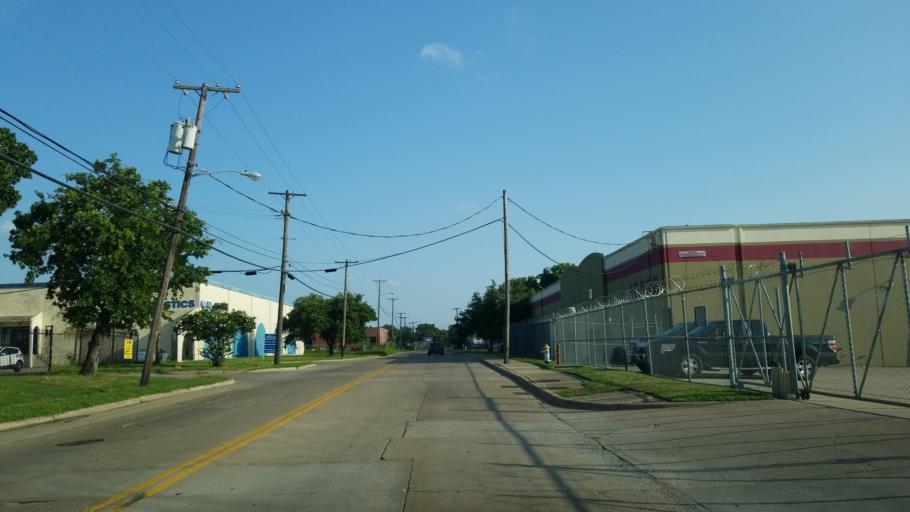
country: US
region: Texas
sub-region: Dallas County
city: Farmers Branch
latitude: 32.8770
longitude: -96.8903
